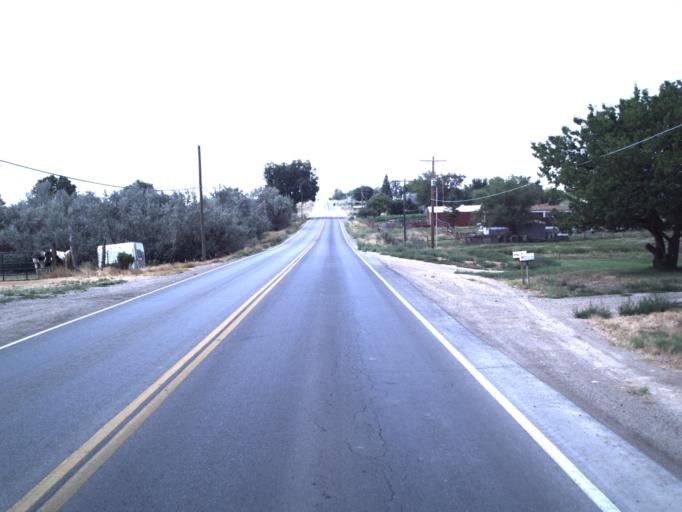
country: US
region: Utah
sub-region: Uintah County
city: Naples
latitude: 40.3927
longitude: -109.4988
